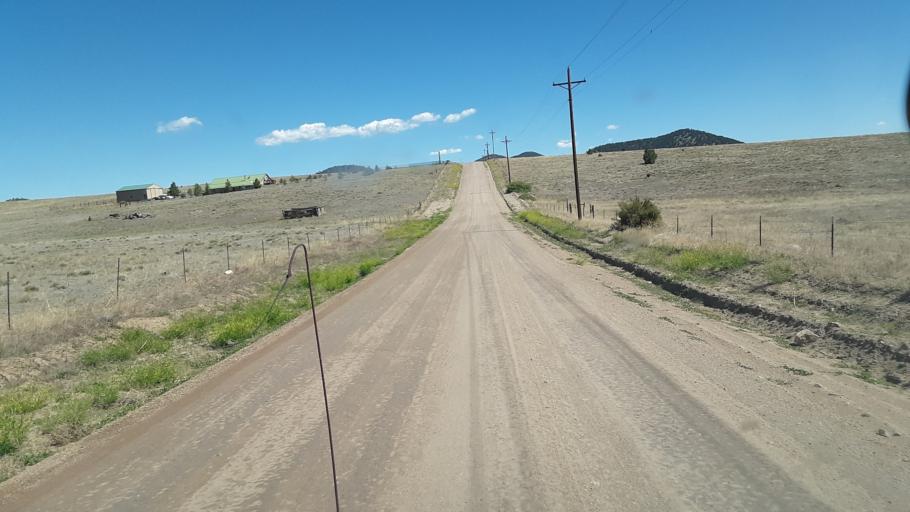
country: US
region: Colorado
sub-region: Custer County
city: Westcliffe
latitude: 38.2789
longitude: -105.5009
